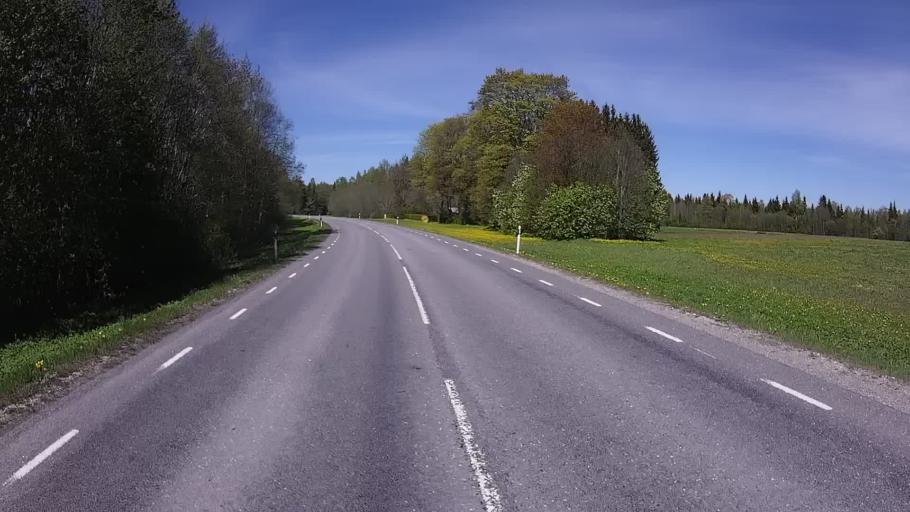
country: EE
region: Raplamaa
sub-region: Kehtna vald
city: Kehtna
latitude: 59.0512
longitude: 25.0221
